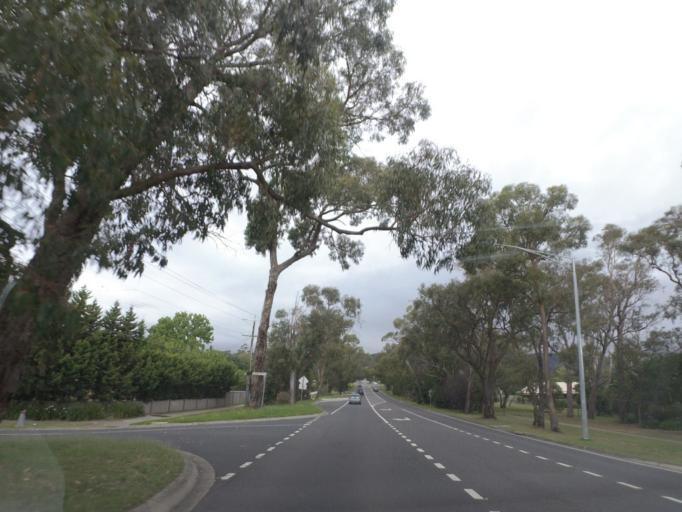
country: AU
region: Victoria
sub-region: Yarra Ranges
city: Kilsyth
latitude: -37.8060
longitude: 145.3226
